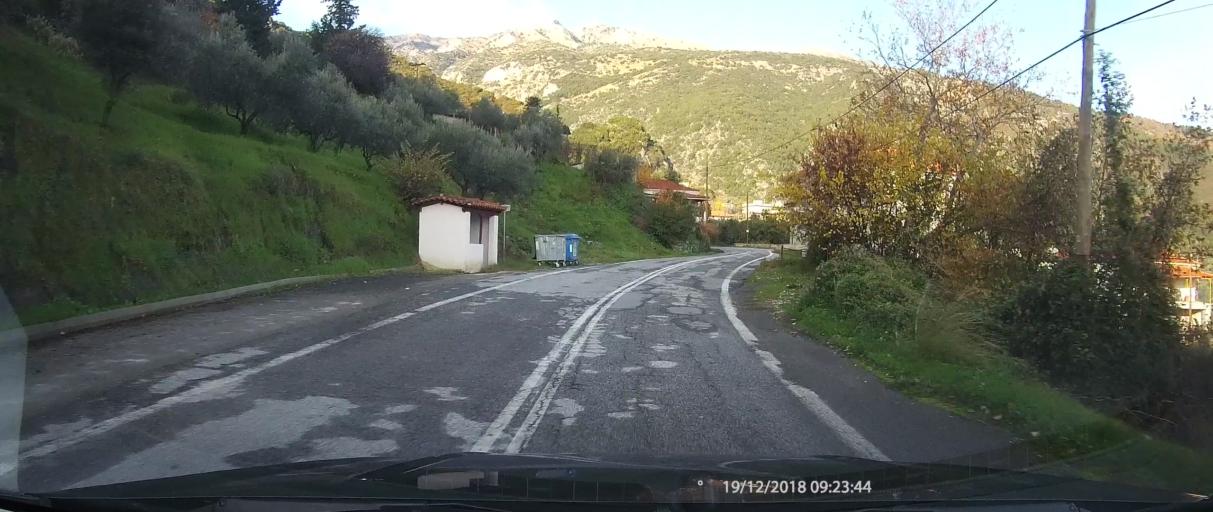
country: GR
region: Peloponnese
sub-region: Nomos Lakonias
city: Magoula
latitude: 37.0944
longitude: 22.3451
